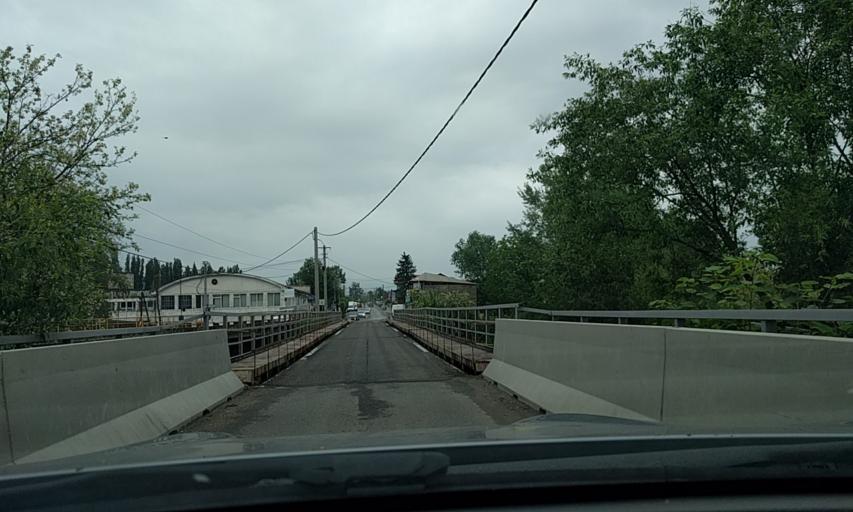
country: RO
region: Dambovita
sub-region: Oras Pucioasa
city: Glodeni
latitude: 45.0437
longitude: 25.4393
